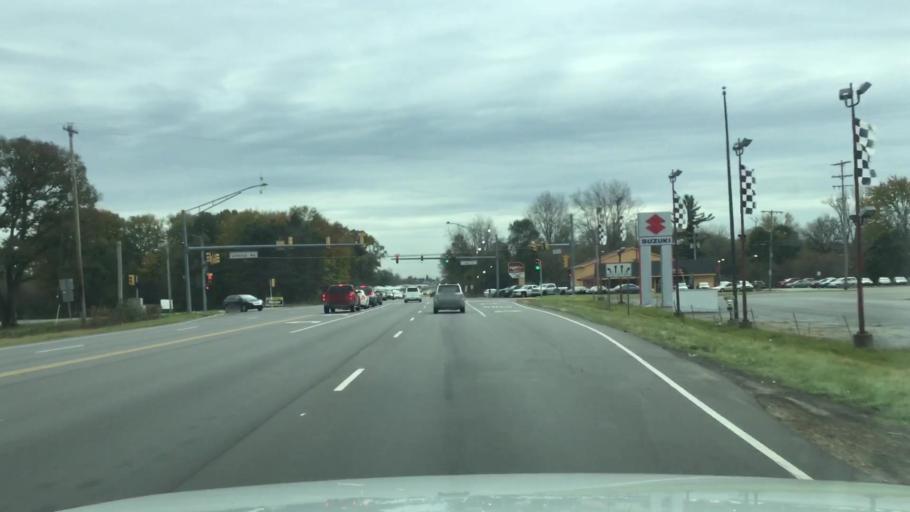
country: US
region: Michigan
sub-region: Kalamazoo County
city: Eastwood
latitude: 42.2841
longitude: -85.5308
